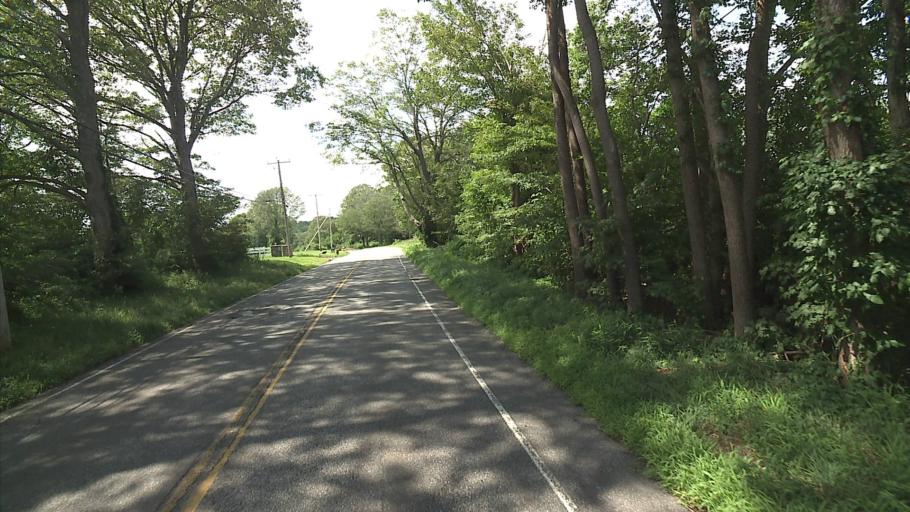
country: US
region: Connecticut
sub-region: New London County
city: Montville Center
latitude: 41.5059
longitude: -72.2424
